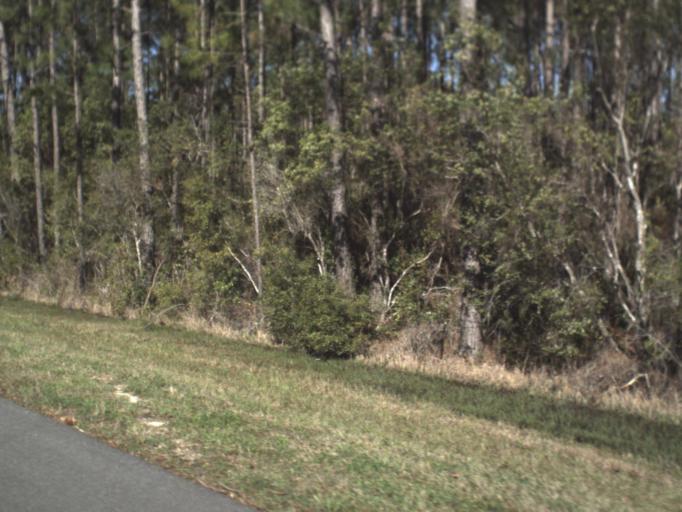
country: US
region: Florida
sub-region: Bay County
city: Callaway
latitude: 30.1527
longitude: -85.5189
